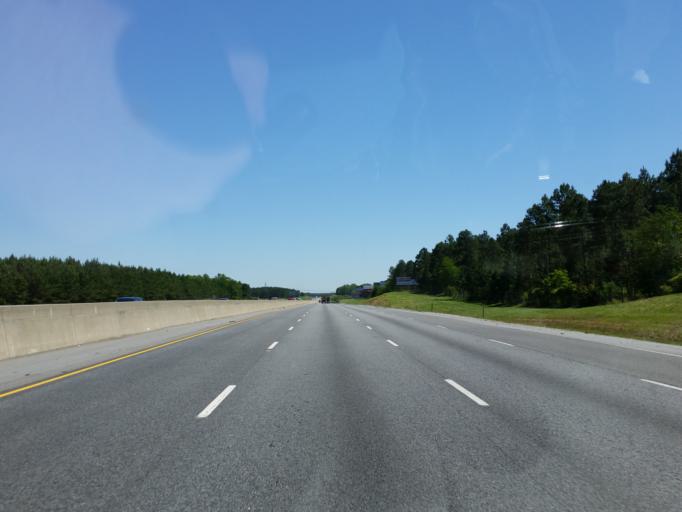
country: US
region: Georgia
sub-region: Tift County
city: Tifton
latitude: 31.5477
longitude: -83.5331
